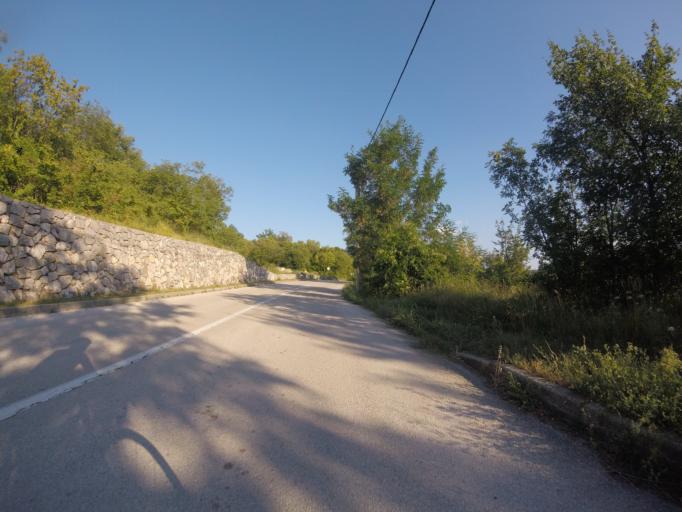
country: HR
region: Primorsko-Goranska
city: Selce
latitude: 45.1832
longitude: 14.7341
